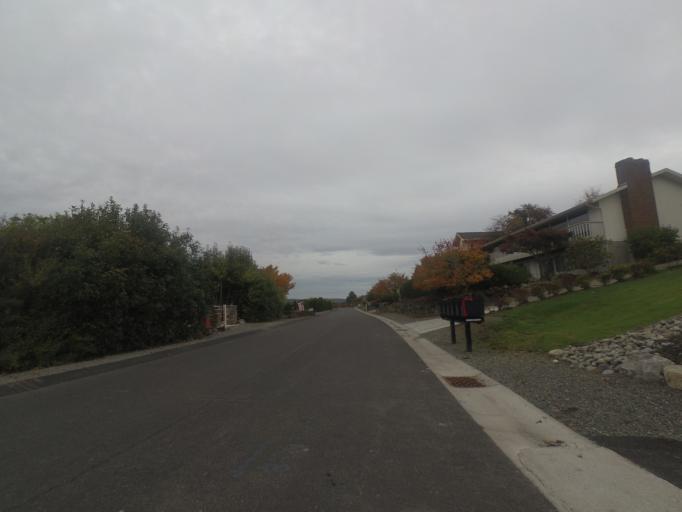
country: US
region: Washington
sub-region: Pierce County
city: University Place
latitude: 47.2299
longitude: -122.5619
